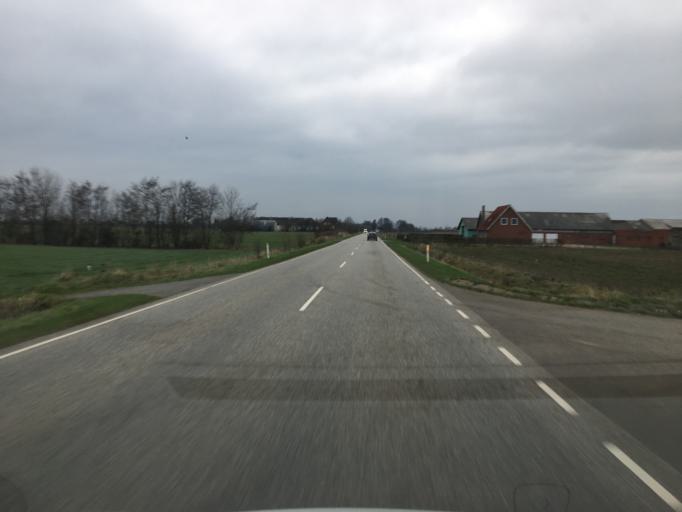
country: DK
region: South Denmark
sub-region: Aabenraa Kommune
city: Rodekro
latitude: 55.0096
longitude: 9.2676
